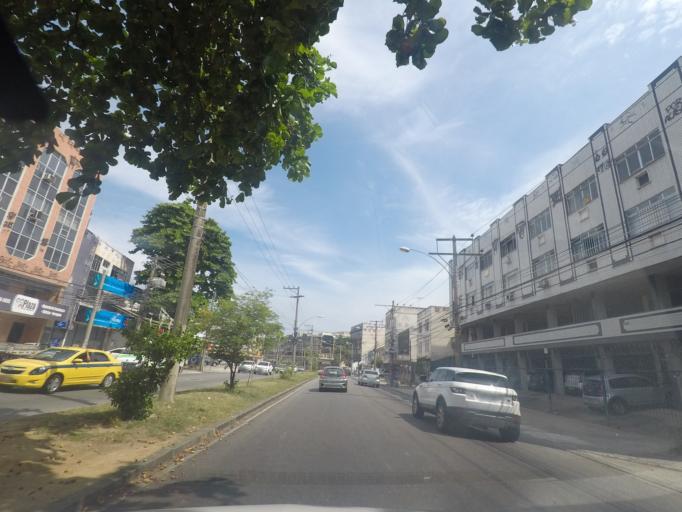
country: BR
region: Rio de Janeiro
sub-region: Rio De Janeiro
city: Rio de Janeiro
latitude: -22.8095
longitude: -43.1956
